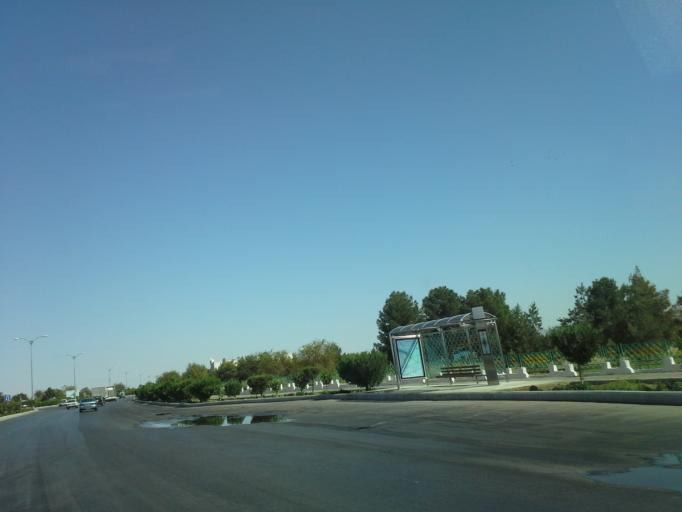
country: TM
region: Ahal
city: Annau
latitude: 37.9114
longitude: 58.4956
